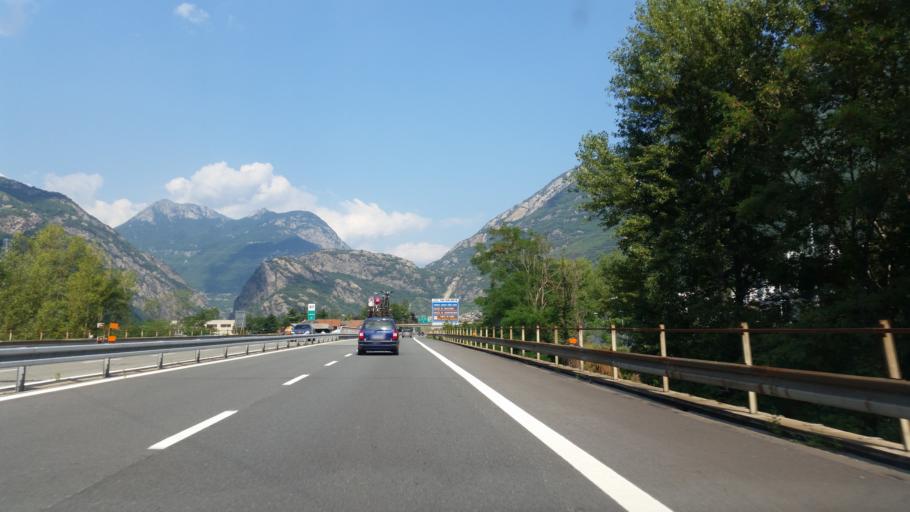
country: IT
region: Aosta Valley
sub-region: Valle d'Aosta
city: Pont-Saint-Martin
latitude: 45.5905
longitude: 7.7923
